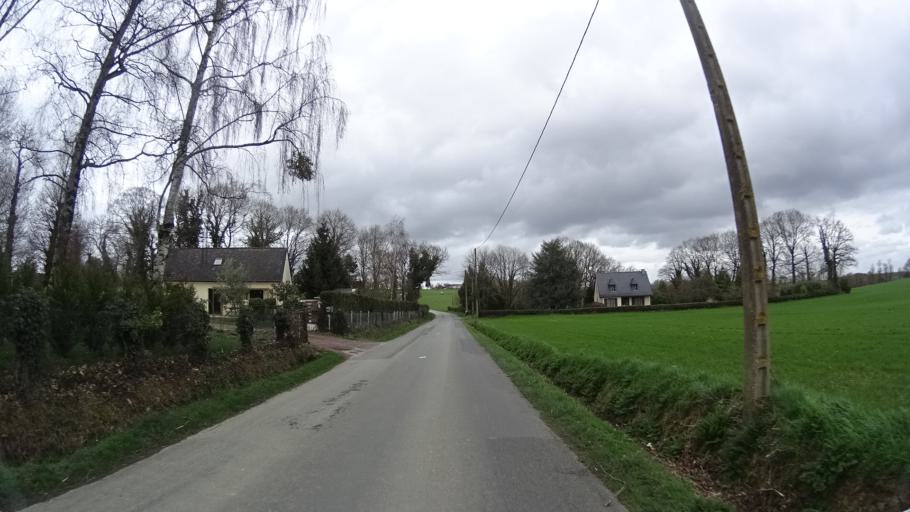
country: FR
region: Brittany
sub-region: Departement d'Ille-et-Vilaine
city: Geveze
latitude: 48.2014
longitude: -1.8302
